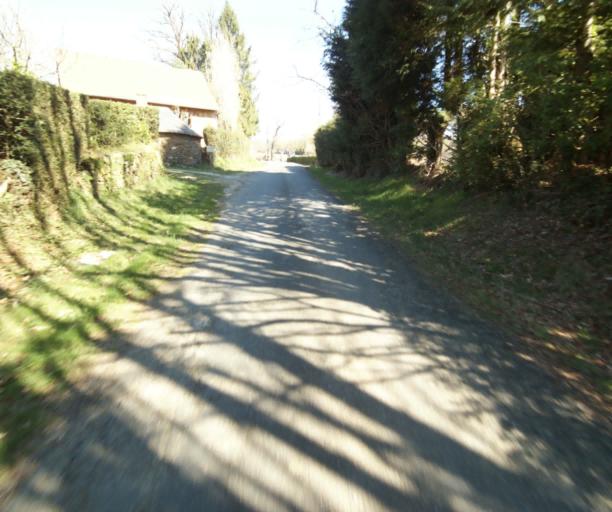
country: FR
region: Limousin
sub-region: Departement de la Correze
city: Saint-Clement
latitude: 45.3504
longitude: 1.6616
